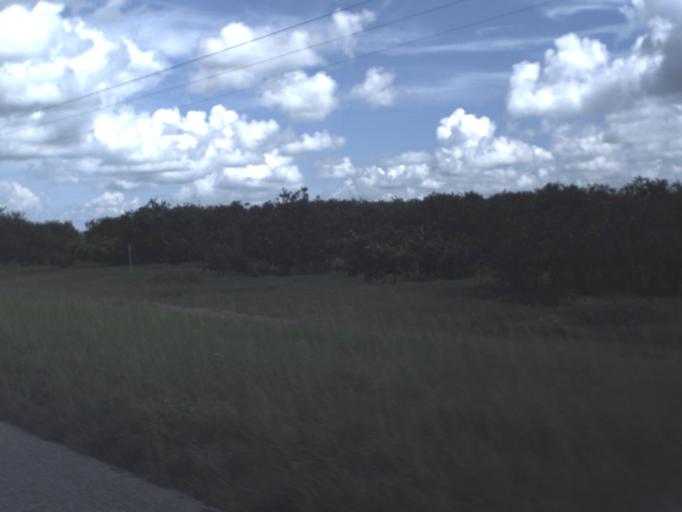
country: US
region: Florida
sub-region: Highlands County
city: Placid Lakes
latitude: 27.1945
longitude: -81.3285
